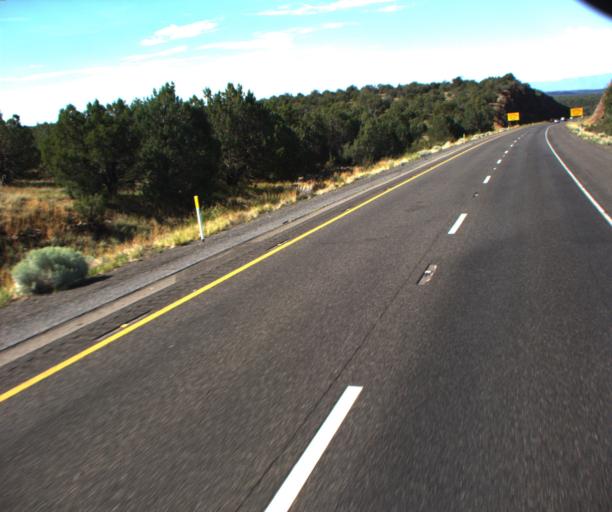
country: US
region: Arizona
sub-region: Yavapai County
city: Village of Oak Creek (Big Park)
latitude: 34.7931
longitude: -111.6014
